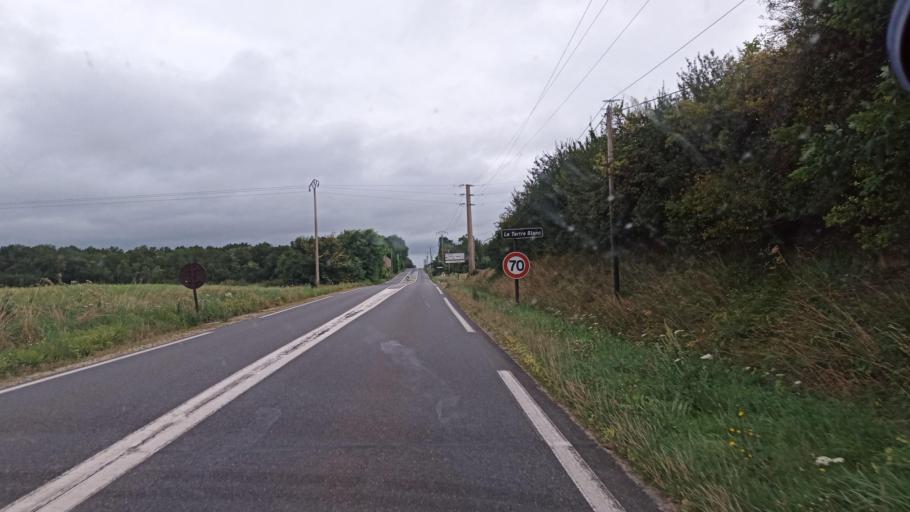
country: FR
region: Ile-de-France
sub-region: Departement de Seine-et-Marne
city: Cannes-Ecluse
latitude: 48.3408
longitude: 2.9580
